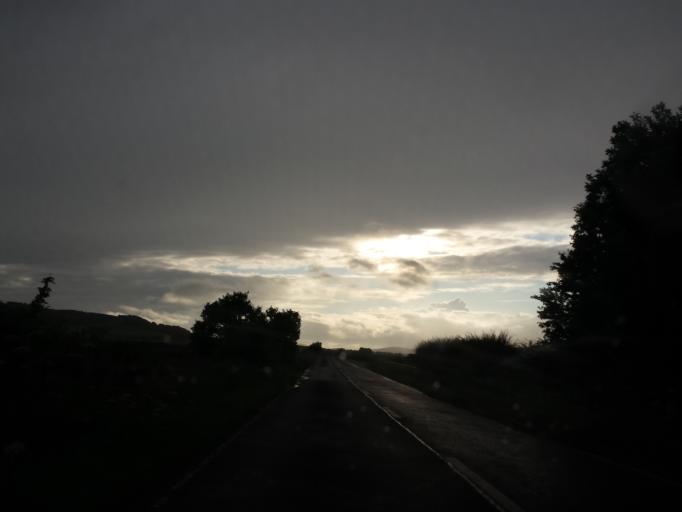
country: GB
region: Scotland
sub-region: Fife
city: Ladybank
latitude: 56.3452
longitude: -3.1018
